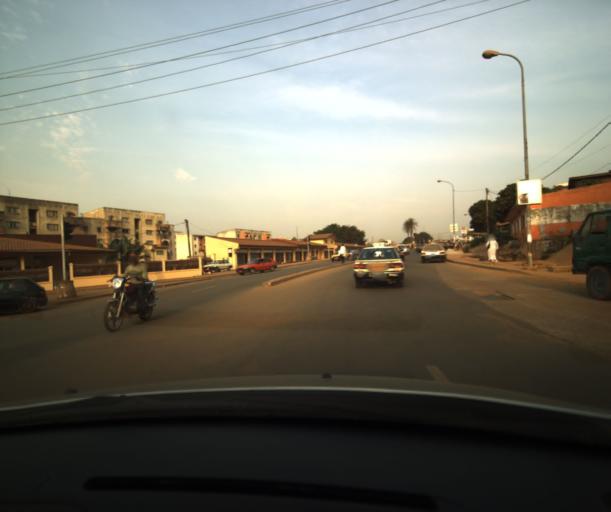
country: CM
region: Centre
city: Yaounde
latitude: 3.8714
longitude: 11.4897
